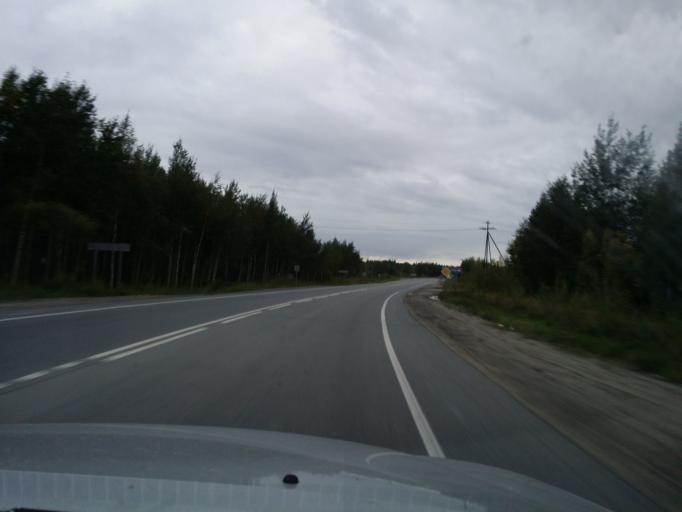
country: RU
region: Khanty-Mansiyskiy Avtonomnyy Okrug
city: Izluchinsk
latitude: 61.0322
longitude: 76.8952
